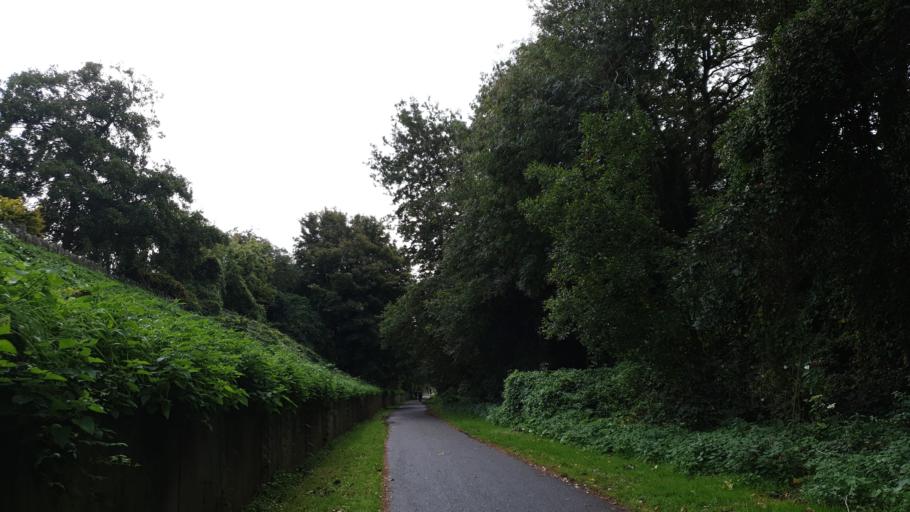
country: IE
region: Munster
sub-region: County Cork
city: Cork
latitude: 51.8954
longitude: -8.4174
